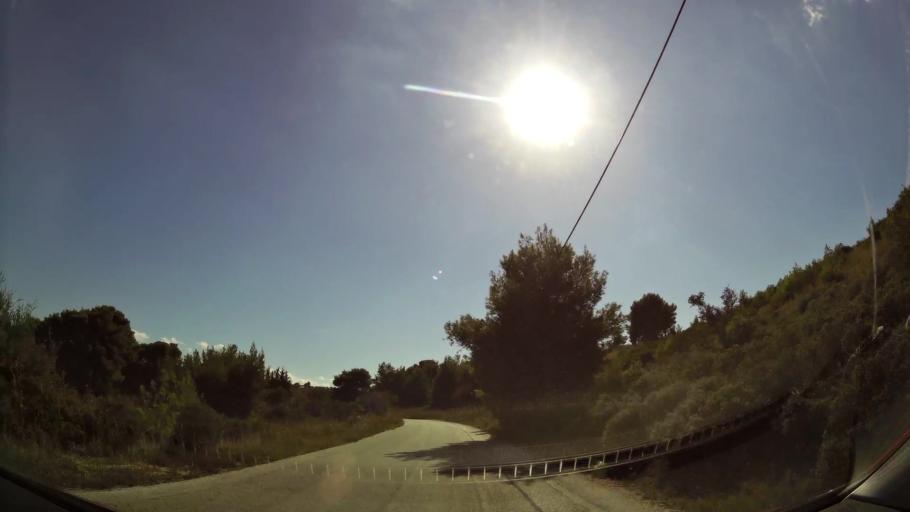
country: GR
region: Attica
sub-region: Nomarchia Anatolikis Attikis
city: Dioni
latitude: 38.0187
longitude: 23.9272
